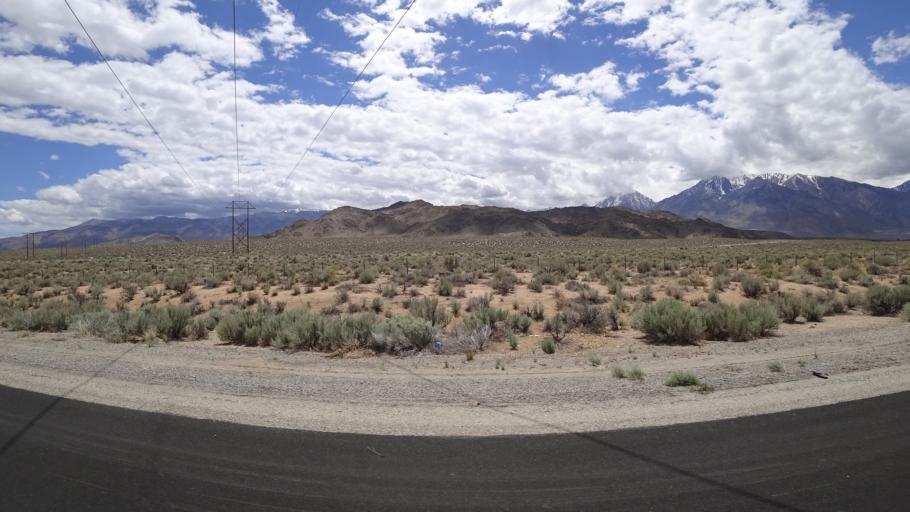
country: US
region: California
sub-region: Inyo County
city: West Bishop
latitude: 37.3959
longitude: -118.5180
